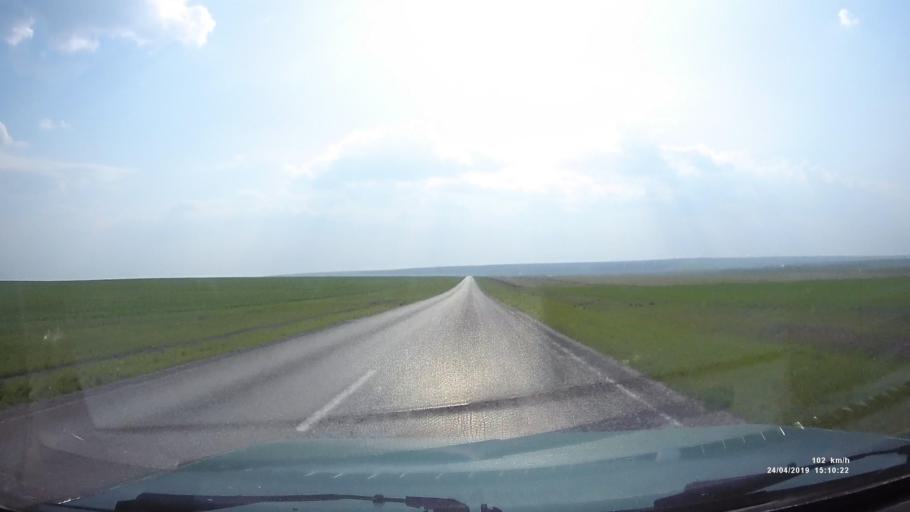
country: RU
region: Rostov
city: Remontnoye
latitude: 46.5504
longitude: 43.3427
